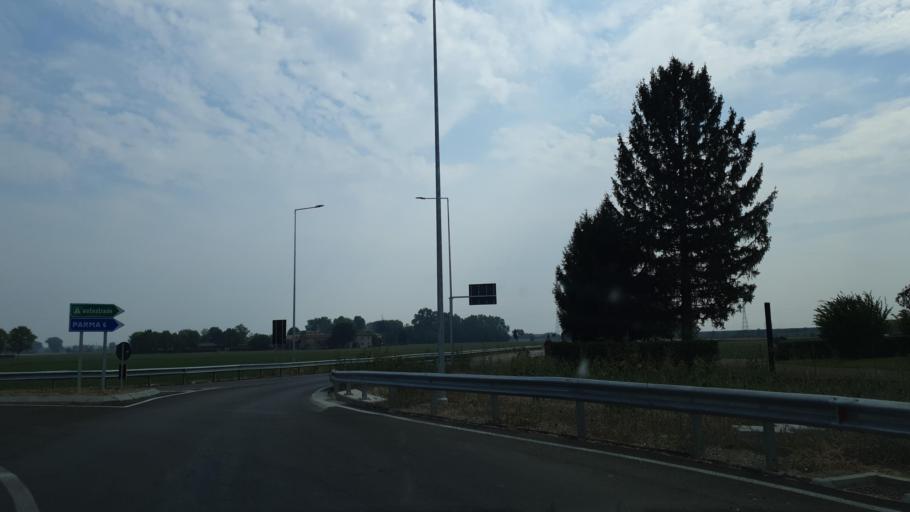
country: IT
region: Emilia-Romagna
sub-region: Provincia di Parma
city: San Secondo Parmense
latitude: 44.8696
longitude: 10.2506
